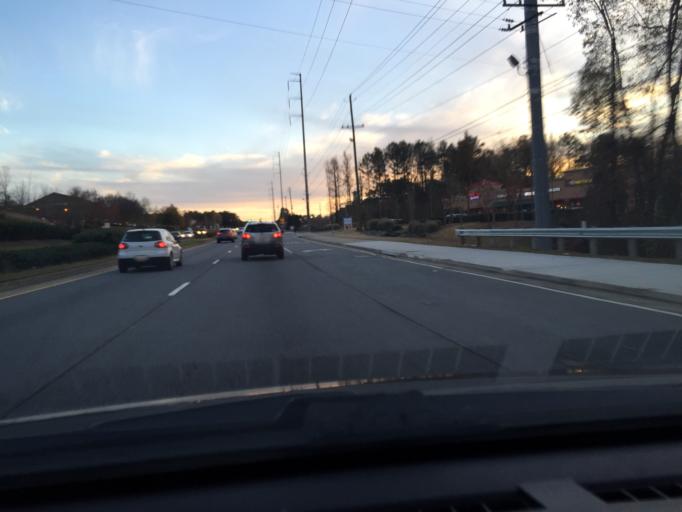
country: US
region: Georgia
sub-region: Fulton County
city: Johns Creek
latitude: 34.0367
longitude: -84.1854
